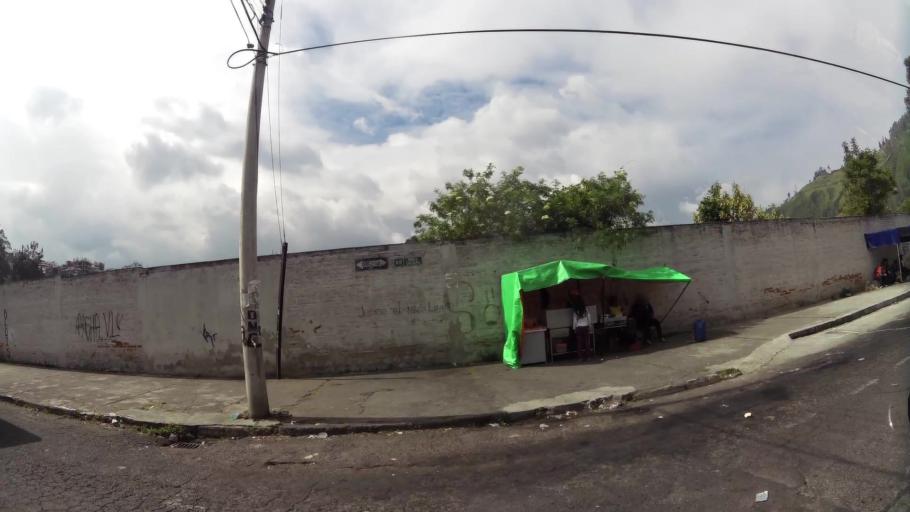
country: EC
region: Pichincha
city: Quito
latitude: -0.2184
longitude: -78.4838
